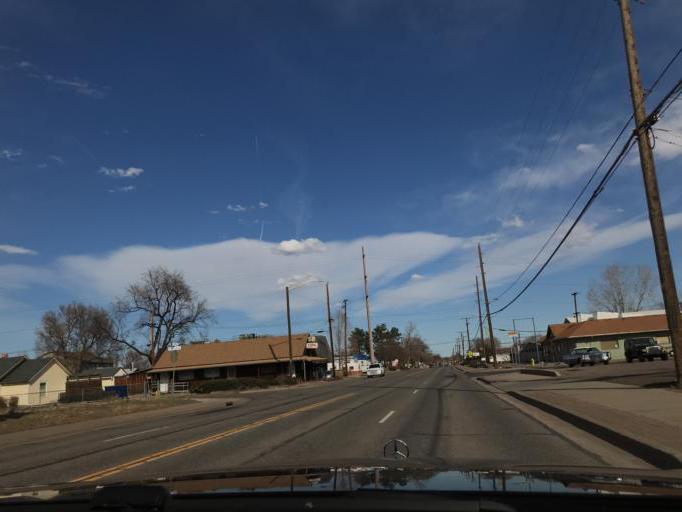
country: US
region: Colorado
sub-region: Jefferson County
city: Arvada
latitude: 39.7781
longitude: -105.1231
